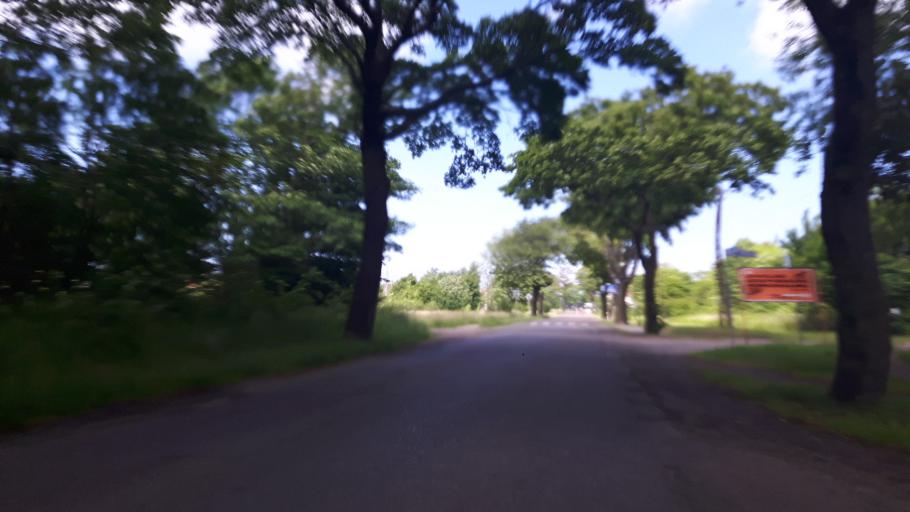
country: PL
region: Pomeranian Voivodeship
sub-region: Powiat slupski
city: Ustka
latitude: 54.5689
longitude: 16.8502
